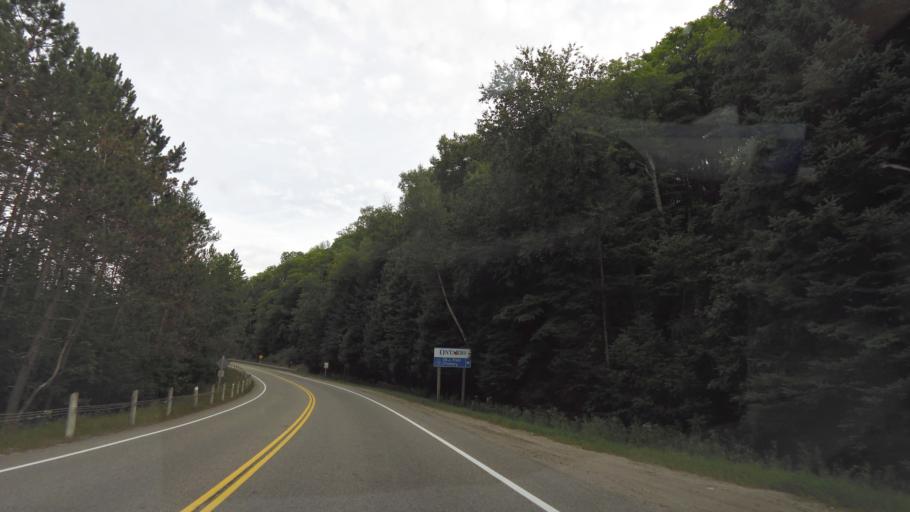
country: CA
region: Ontario
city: Bancroft
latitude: 45.0445
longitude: -78.4955
